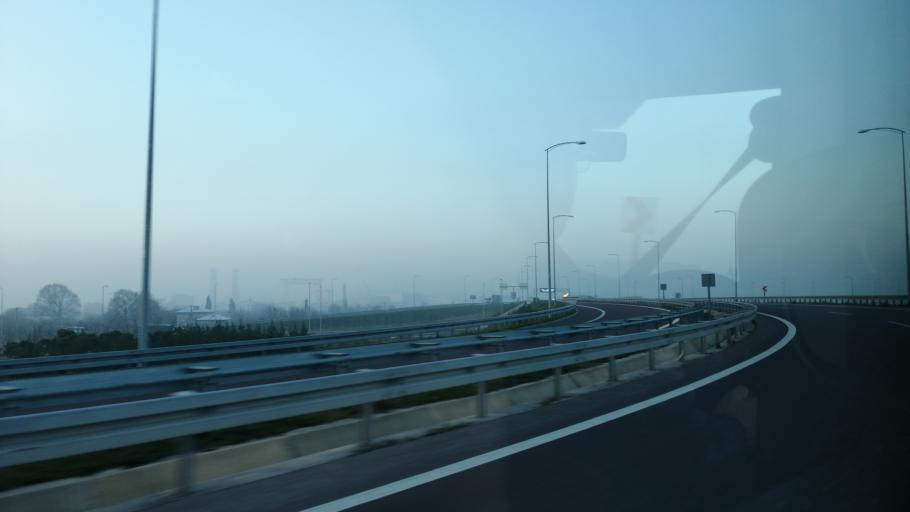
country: TR
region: Yalova
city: Altinova
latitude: 40.6892
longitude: 29.4706
